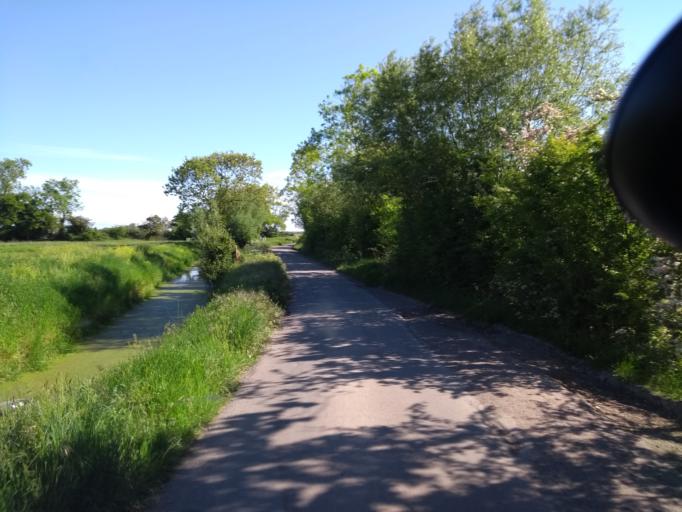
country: GB
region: England
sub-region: Somerset
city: Bridgwater
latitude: 51.1476
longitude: -3.0198
